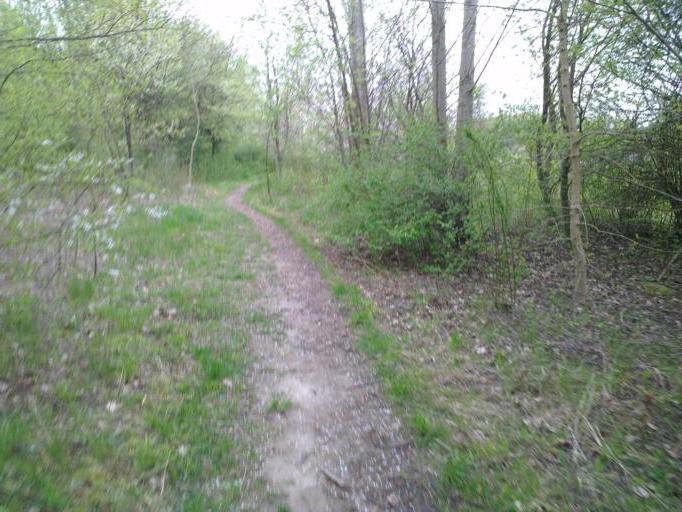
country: DK
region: Capital Region
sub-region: Frederikssund Kommune
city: Frederikssund
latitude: 55.8431
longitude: 12.0803
